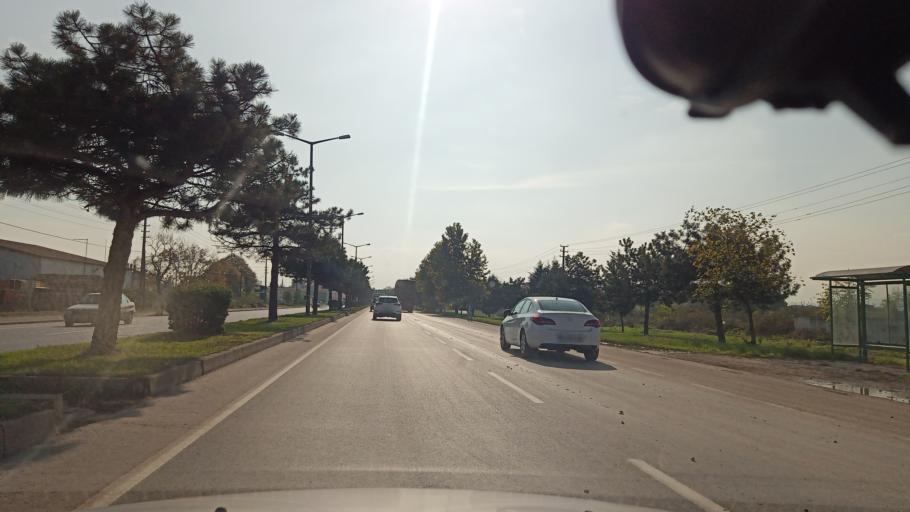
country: TR
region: Sakarya
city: Adapazari
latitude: 40.8066
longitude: 30.4056
